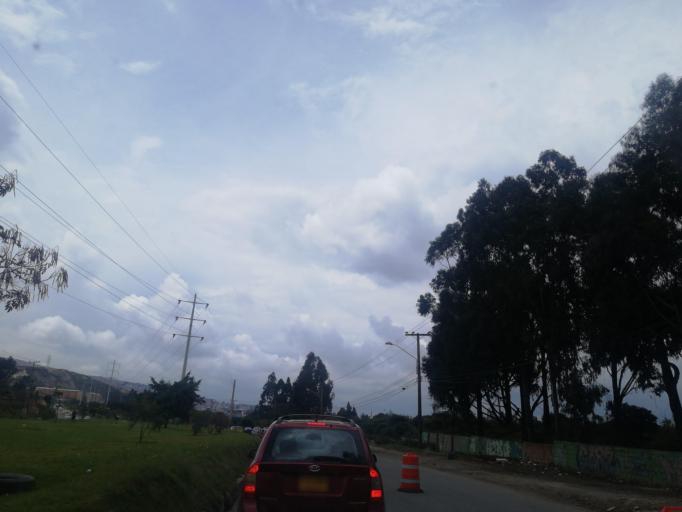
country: CO
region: Bogota D.C.
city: Bogota
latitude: 4.5353
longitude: -74.1278
